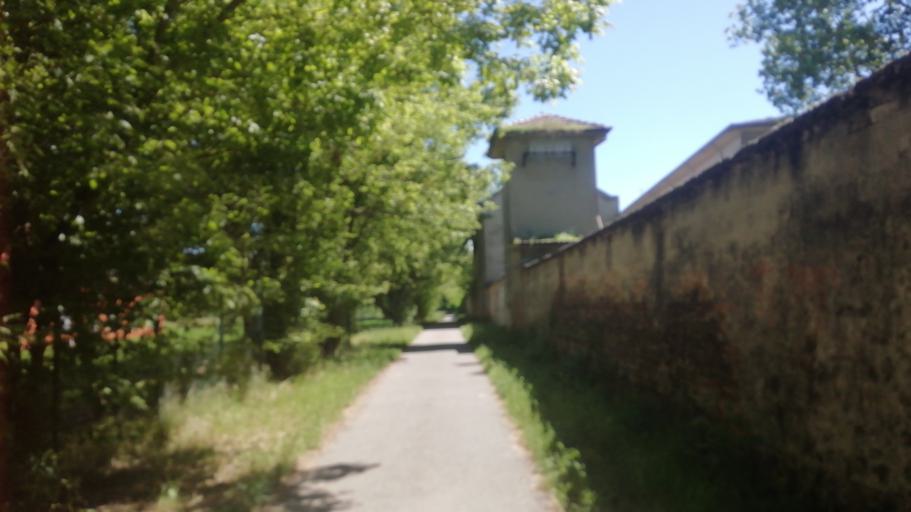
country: IT
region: Emilia-Romagna
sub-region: Provincia di Piacenza
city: Borgonovo Valtidone
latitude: 45.0085
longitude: 9.4463
